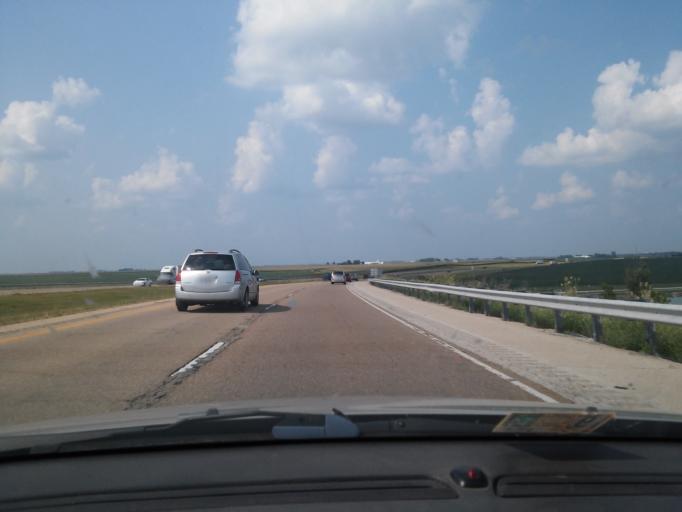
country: US
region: Illinois
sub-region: McLean County
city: Chenoa
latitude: 40.7463
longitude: -88.7375
